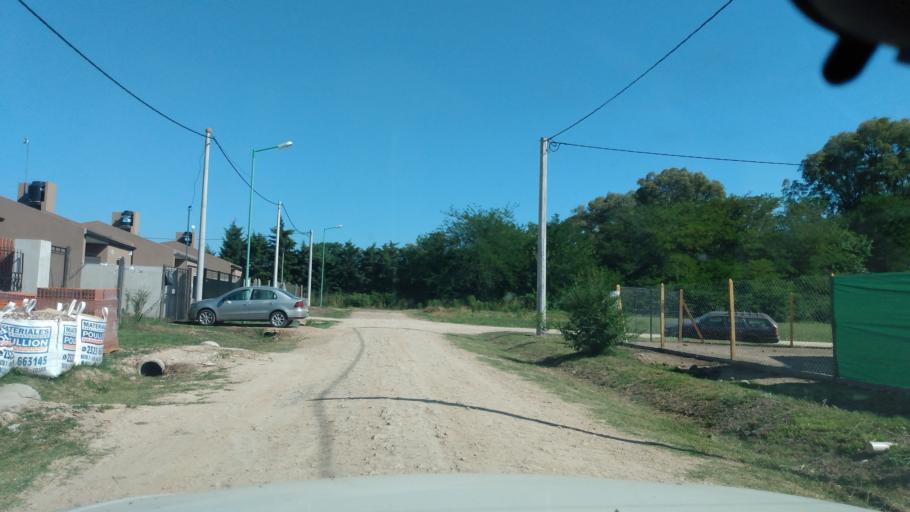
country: AR
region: Buenos Aires
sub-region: Partido de Lujan
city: Lujan
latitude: -34.5527
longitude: -59.1374
